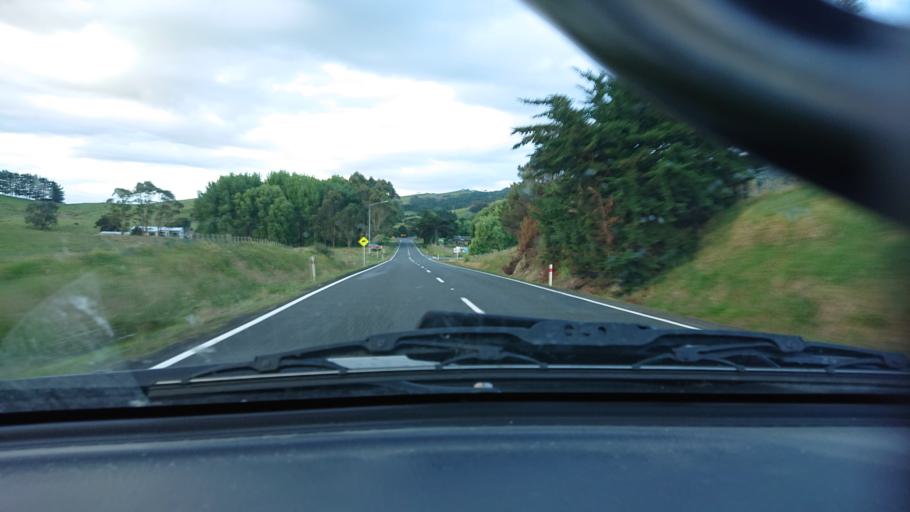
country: NZ
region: Auckland
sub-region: Auckland
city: Parakai
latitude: -36.4659
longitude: 174.4461
